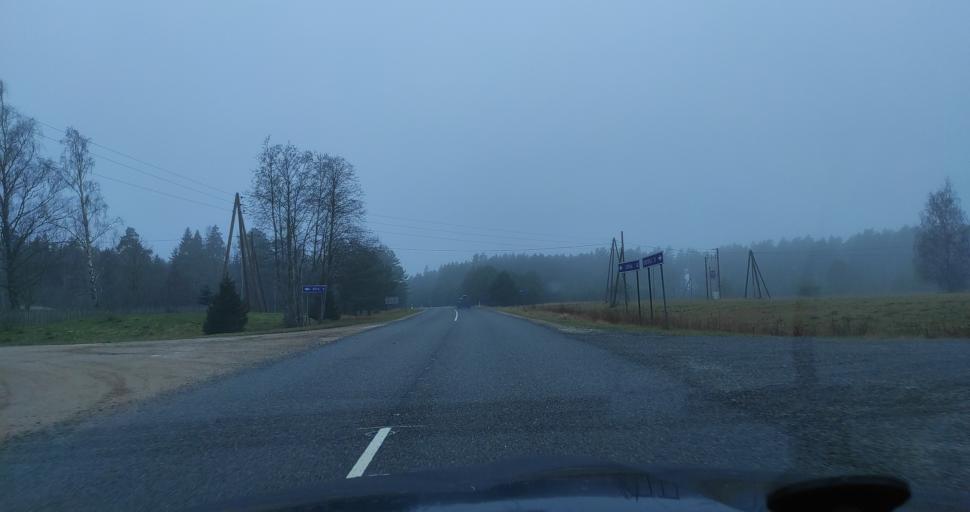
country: LV
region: Pavilostas
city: Pavilosta
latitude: 56.9719
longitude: 21.3473
